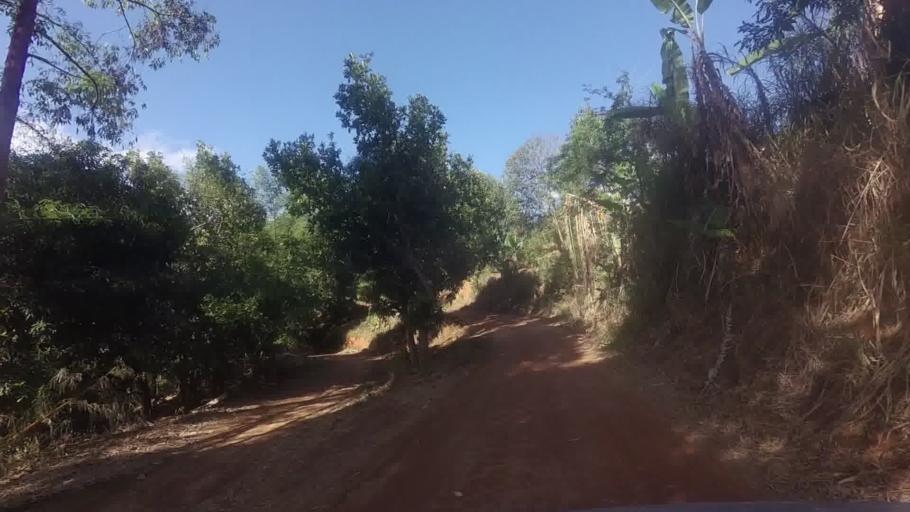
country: BR
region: Espirito Santo
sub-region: Sao Jose Do Calcado
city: Sao Jose do Calcado
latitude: -21.0259
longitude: -41.5749
